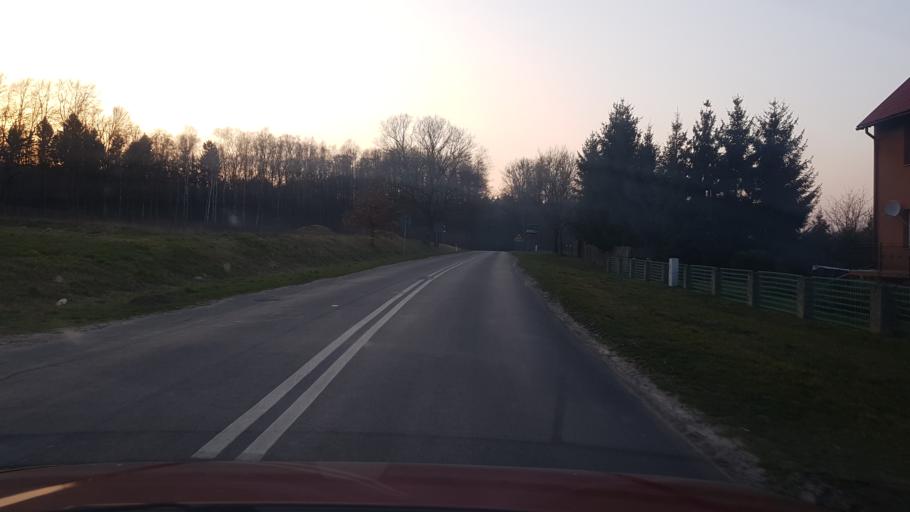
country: PL
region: West Pomeranian Voivodeship
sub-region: Powiat lobeski
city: Radowo Male
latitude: 53.6514
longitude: 15.5244
